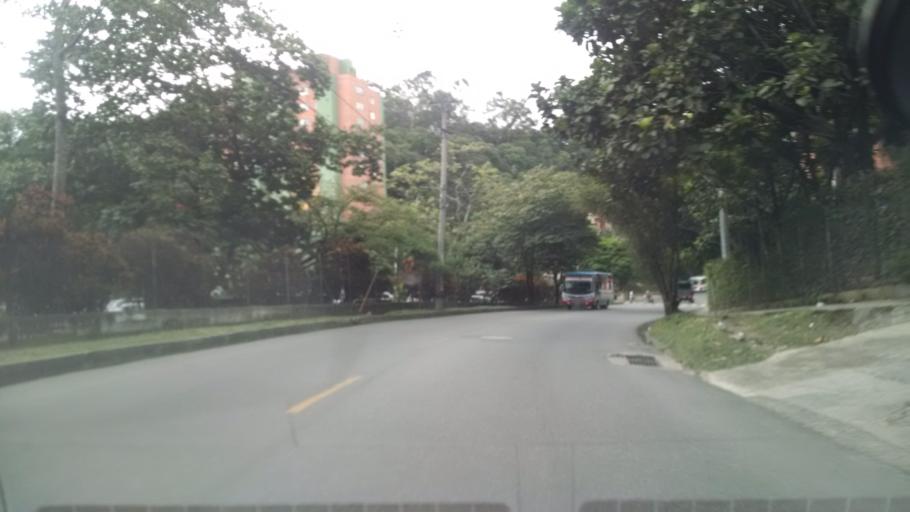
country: CO
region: Antioquia
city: Medellin
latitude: 6.2709
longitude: -75.5882
